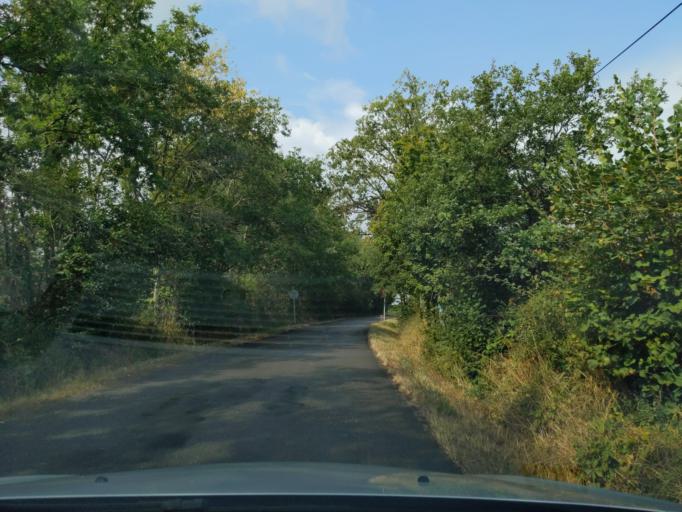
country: FR
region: Bourgogne
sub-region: Departement de Saone-et-Loire
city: Bourbon-Lancy
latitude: 46.6402
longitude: 3.7437
